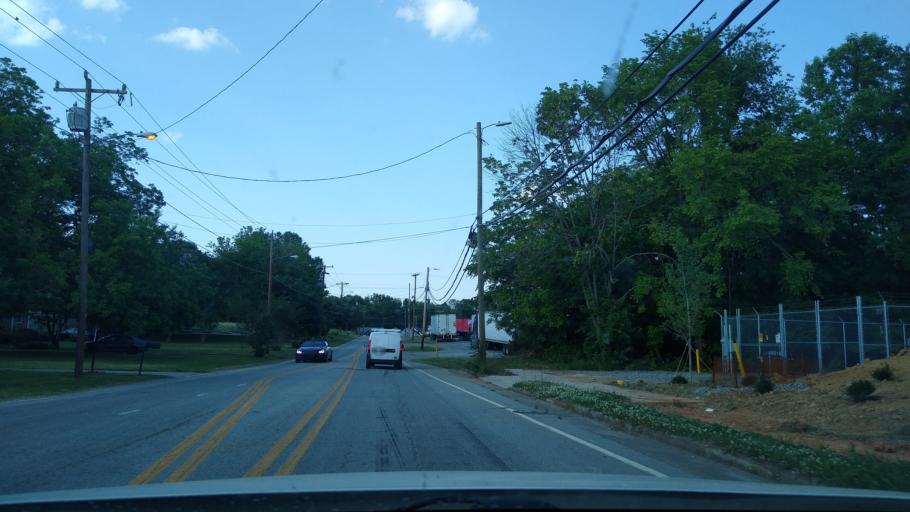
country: US
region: North Carolina
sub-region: Guilford County
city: Greensboro
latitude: 36.0291
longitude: -79.7693
